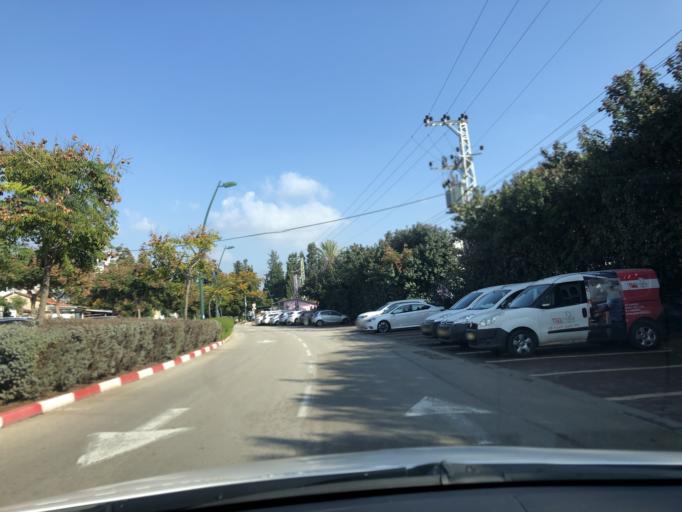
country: IL
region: Tel Aviv
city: Ramat HaSharon
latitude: 32.1265
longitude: 34.8553
